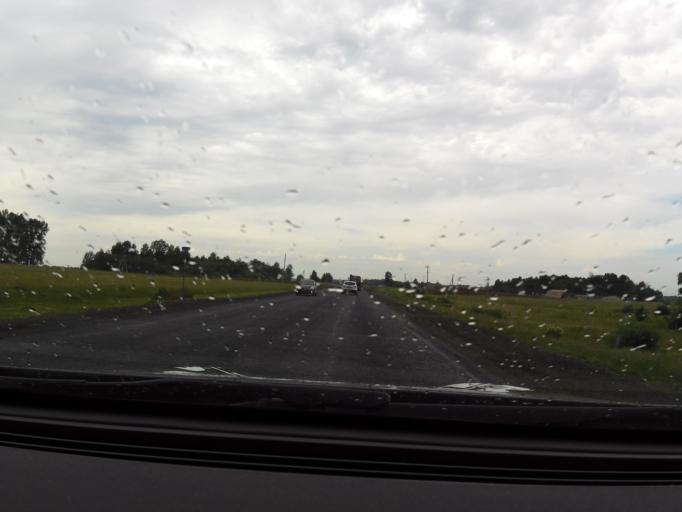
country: RU
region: Bashkortostan
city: Iglino
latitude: 54.7818
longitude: 56.5140
